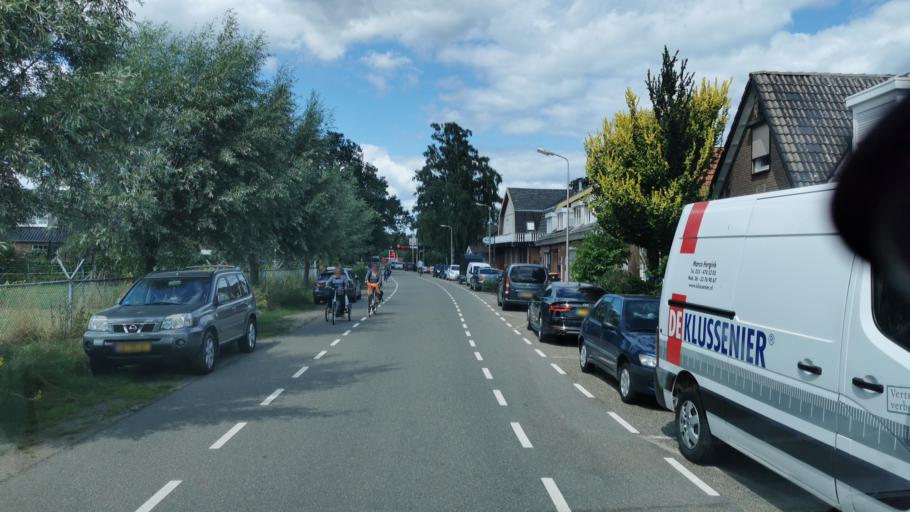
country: NL
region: Overijssel
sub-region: Gemeente Losser
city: Losser
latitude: 52.2333
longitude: 7.0033
